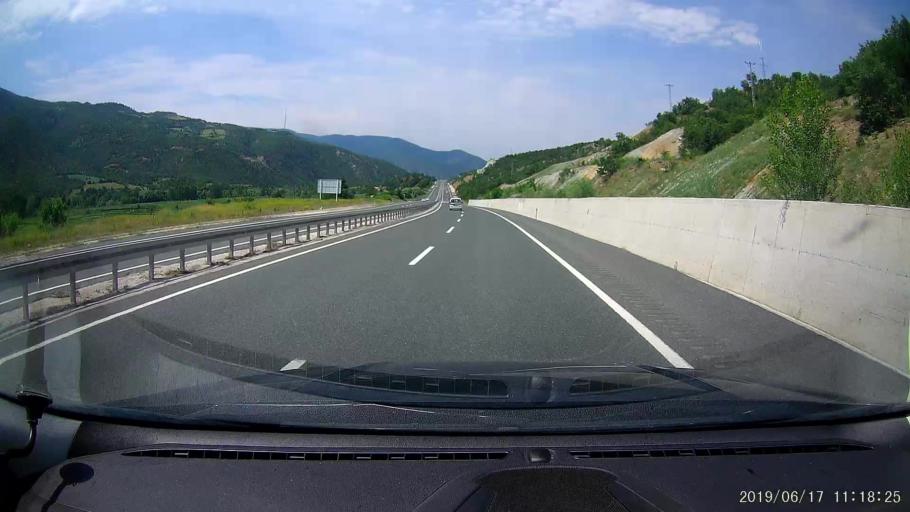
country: TR
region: Cankiri
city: Yaprakli
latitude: 40.9353
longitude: 33.8501
